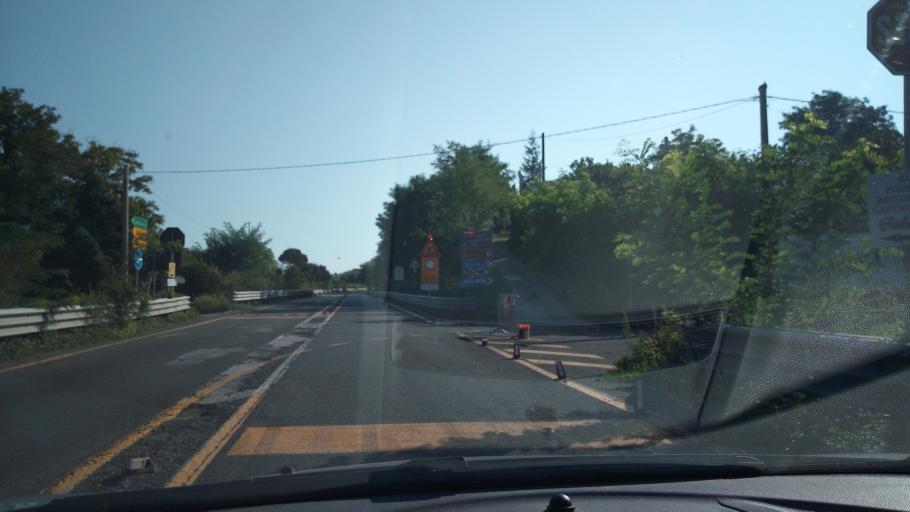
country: IT
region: Campania
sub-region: Provincia di Avellino
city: San Potito Ultra
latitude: 40.9320
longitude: 14.8736
